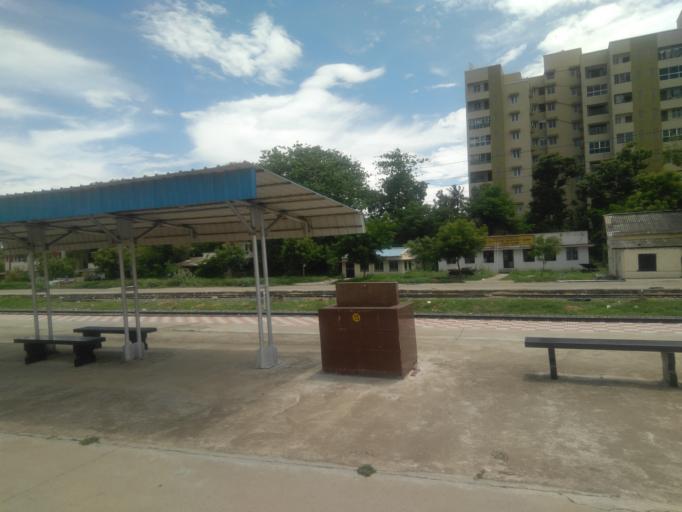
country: IN
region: Tamil Nadu
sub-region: Coimbatore
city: Coimbatore
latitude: 11.0218
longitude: 76.9542
